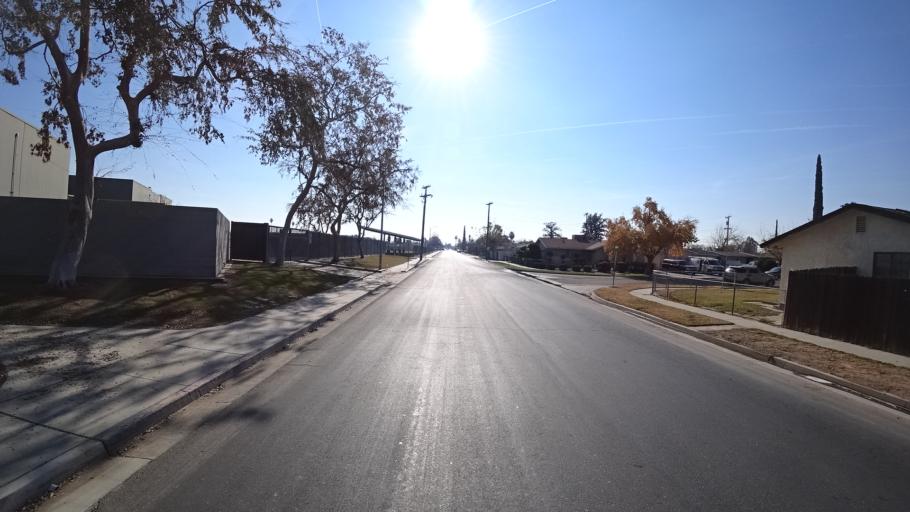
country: US
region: California
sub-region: Kern County
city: Bakersfield
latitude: 35.3234
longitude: -119.0163
